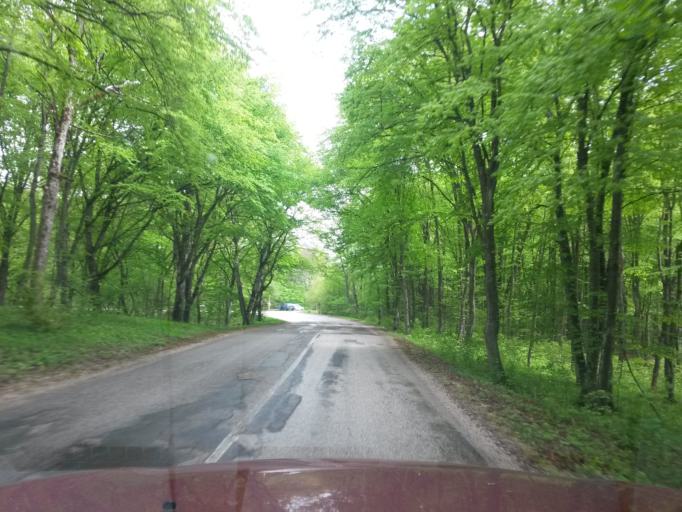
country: SK
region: Kosicky
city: Roznava
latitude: 48.5596
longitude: 20.4798
